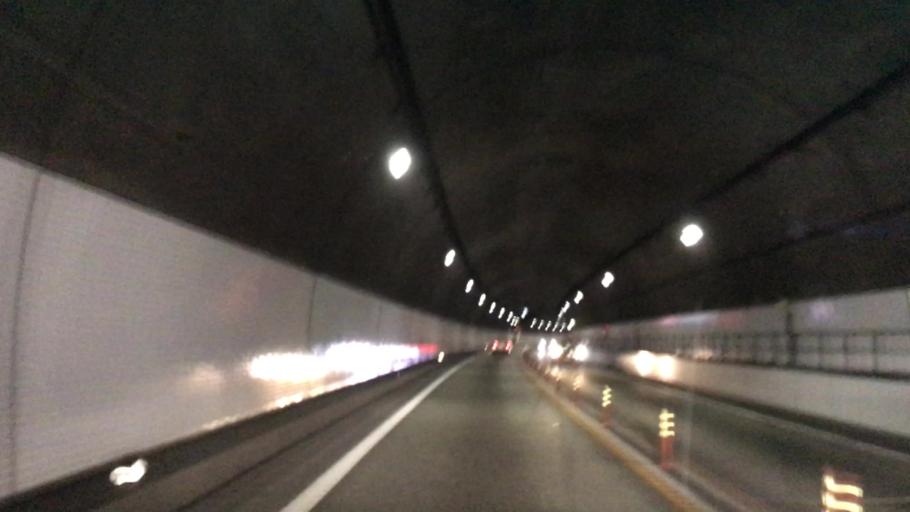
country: JP
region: Hokkaido
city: Iwamizawa
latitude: 42.9348
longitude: 142.0930
